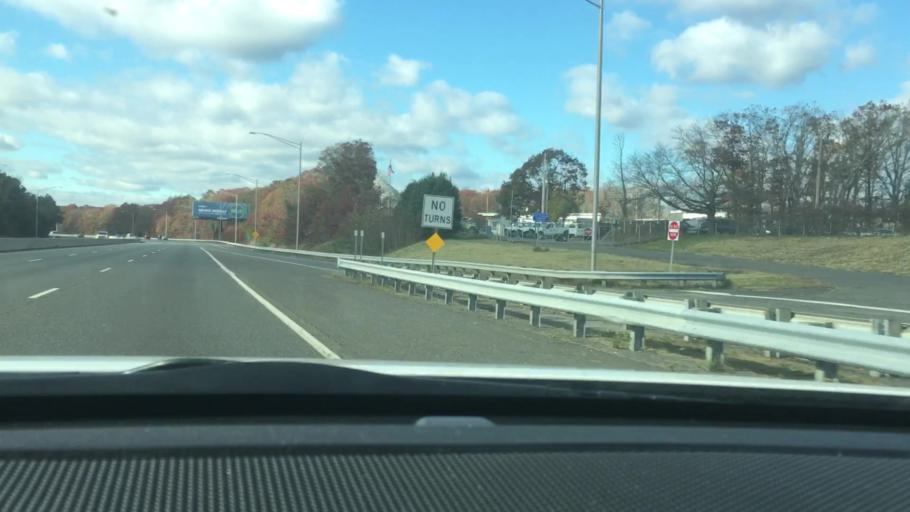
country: US
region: New Jersey
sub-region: Atlantic County
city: Pleasantville
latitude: 39.4037
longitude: -74.5269
